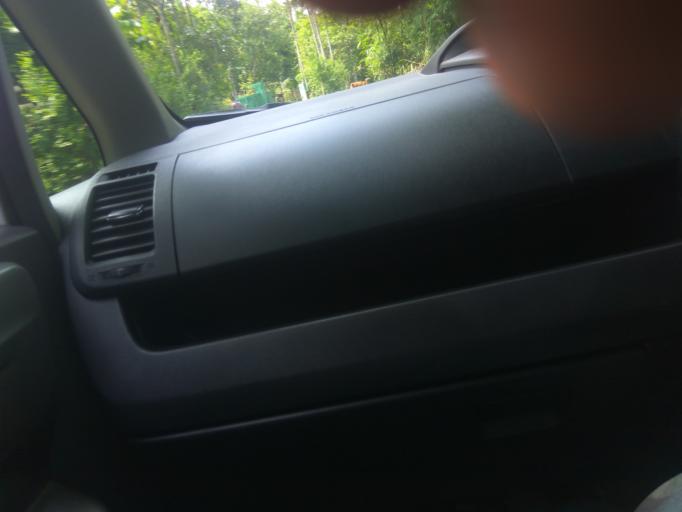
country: IN
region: Assam
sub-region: Karimganj
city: Karimganj
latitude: 24.8113
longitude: 92.1817
